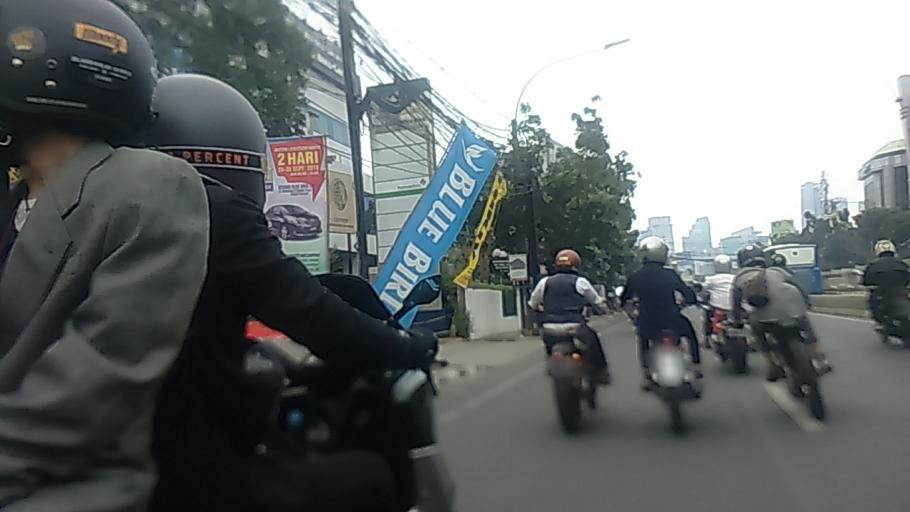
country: ID
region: Jakarta Raya
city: Jakarta
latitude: -6.2474
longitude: 106.8262
